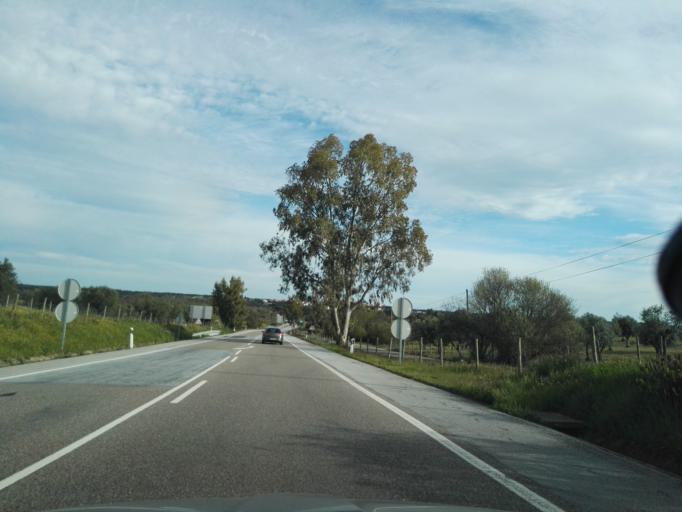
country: PT
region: Portalegre
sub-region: Nisa
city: Nisa
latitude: 39.4388
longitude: -7.7264
